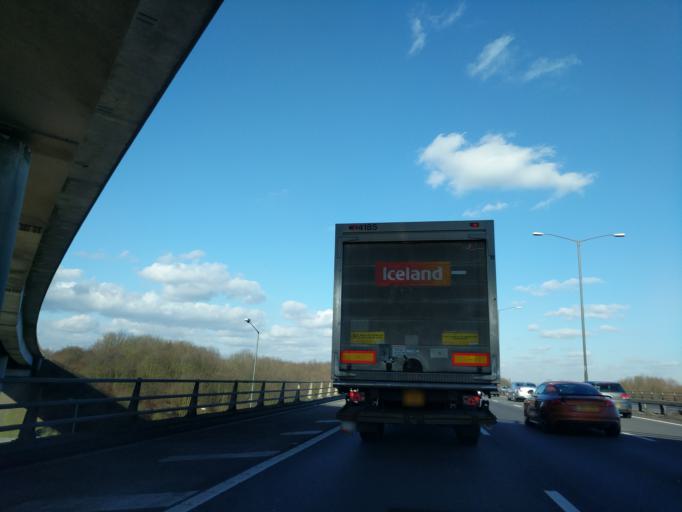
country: GB
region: England
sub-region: Buckinghamshire
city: Iver
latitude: 51.4945
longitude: -0.4943
